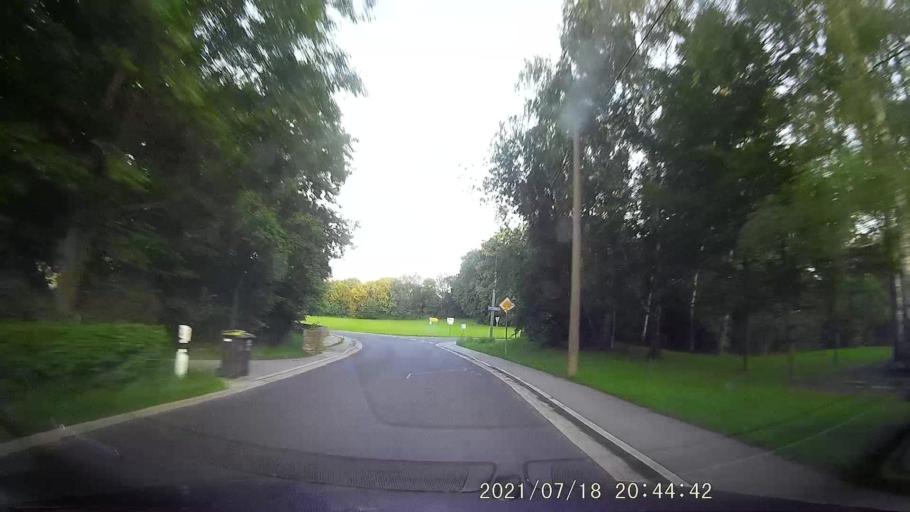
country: DE
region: Saxony
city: Reichenbach
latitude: 51.1965
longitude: 14.7766
